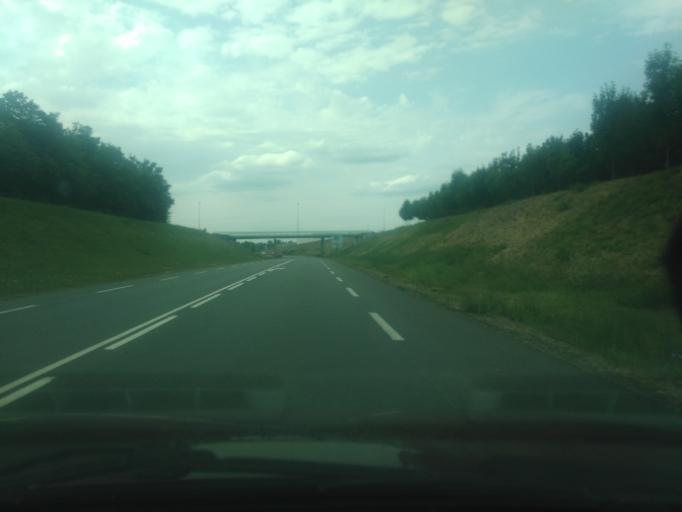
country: FR
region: Pays de la Loire
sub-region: Departement de la Vendee
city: Chantonnay
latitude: 46.6957
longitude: -1.0404
